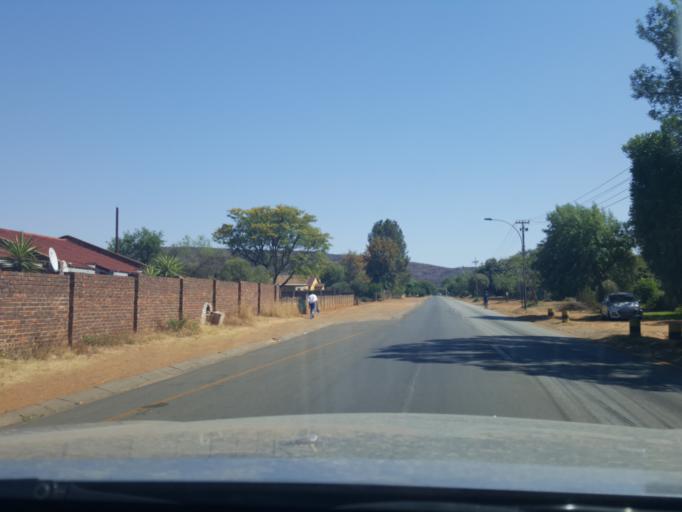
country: ZA
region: North-West
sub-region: Ngaka Modiri Molema District Municipality
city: Zeerust
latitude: -25.5322
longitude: 26.0761
